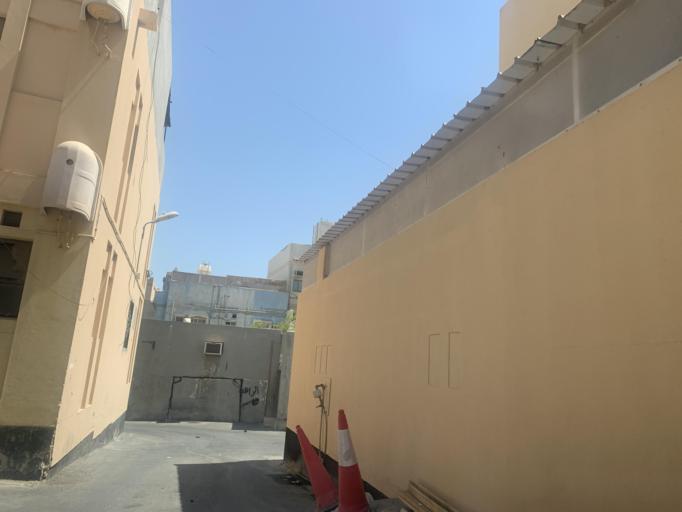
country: BH
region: Muharraq
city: Al Muharraq
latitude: 26.2840
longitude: 50.6251
